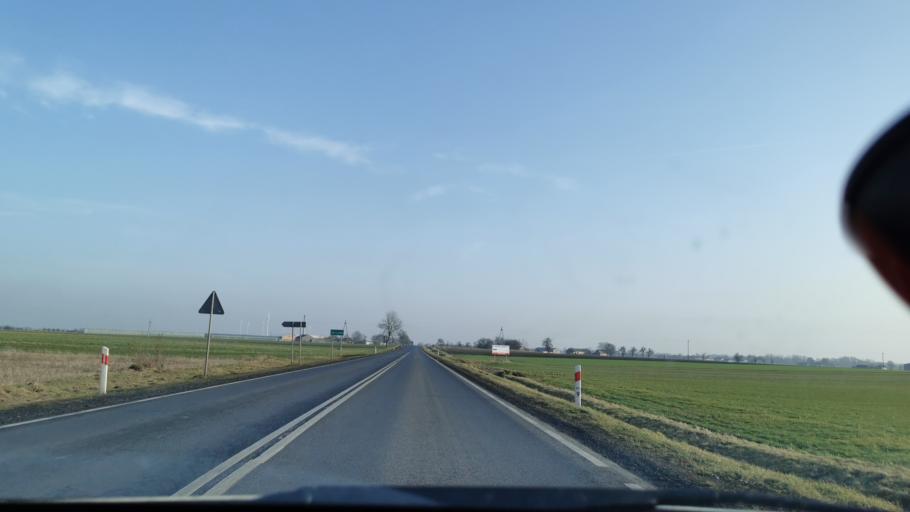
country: PL
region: Lodz Voivodeship
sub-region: Powiat sieradzki
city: Blaszki
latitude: 51.6830
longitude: 18.3357
